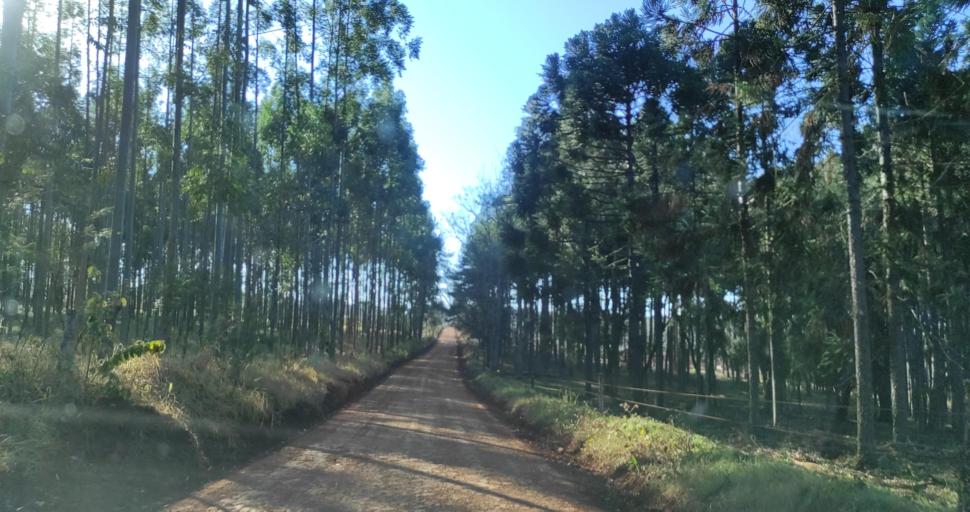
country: AR
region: Misiones
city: Capiovi
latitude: -26.8801
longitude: -55.0241
